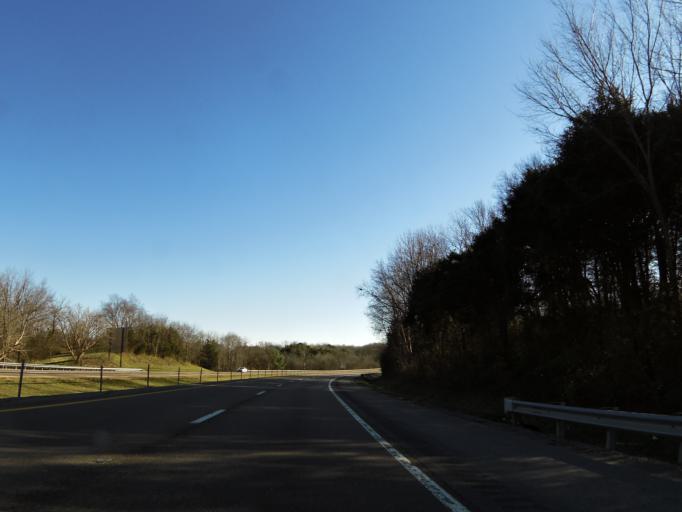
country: US
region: Tennessee
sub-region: Cocke County
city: Newport
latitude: 35.9684
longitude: -83.2313
